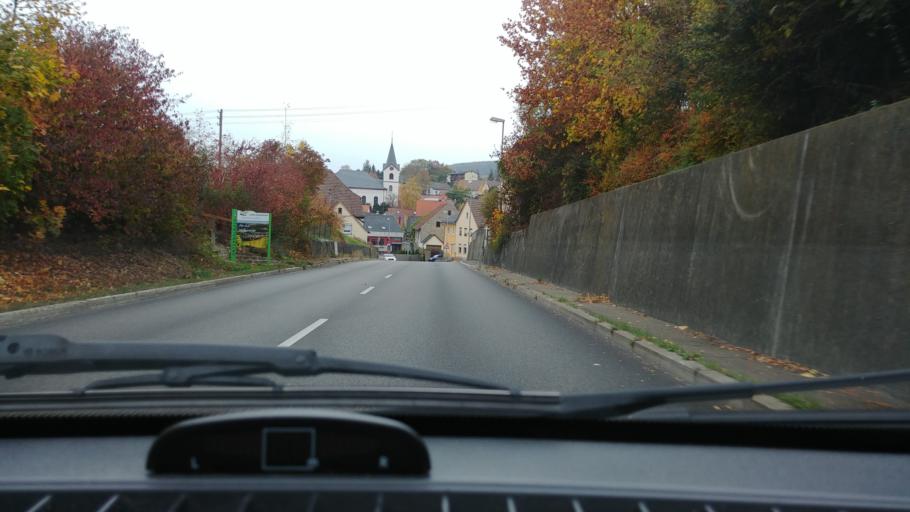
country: DE
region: Baden-Wuerttemberg
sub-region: Regierungsbezirk Stuttgart
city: Bad Mergentheim
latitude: 49.5258
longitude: 9.7483
